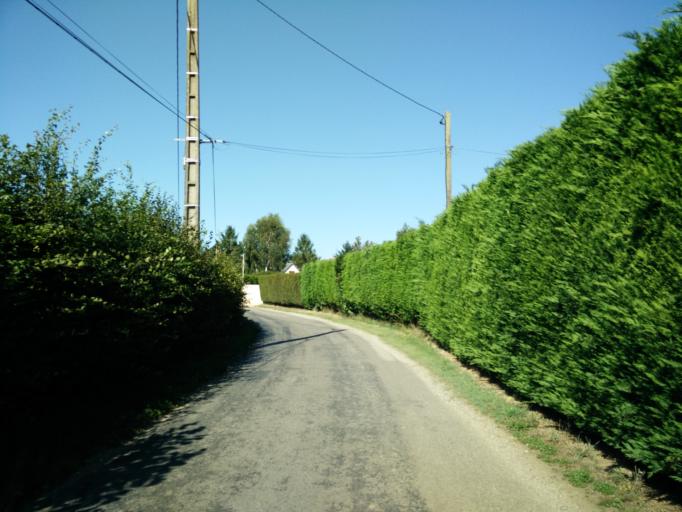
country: FR
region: Haute-Normandie
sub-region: Departement de l'Eure
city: Saint-Pierre-des-Fleurs
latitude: 49.1810
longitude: 0.9823
